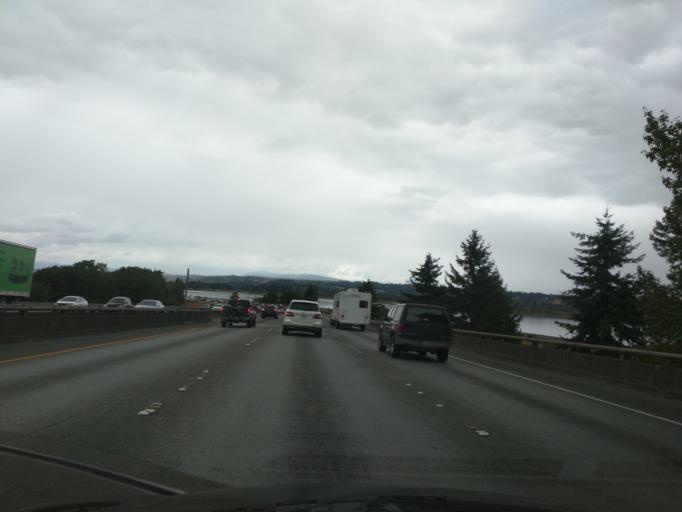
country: US
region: Washington
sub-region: Snohomish County
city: Everett
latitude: 47.9949
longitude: -122.1776
